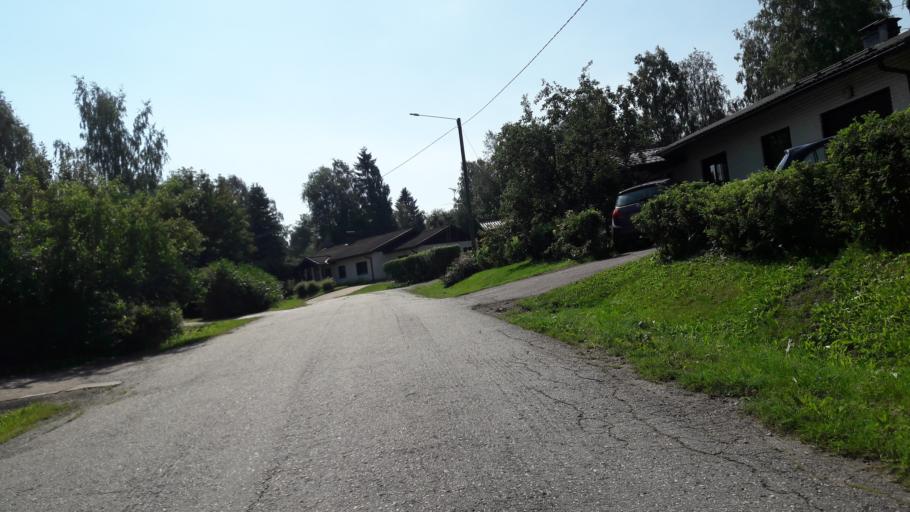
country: FI
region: North Karelia
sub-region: Joensuu
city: Joensuu
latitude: 62.5333
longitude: 29.8357
